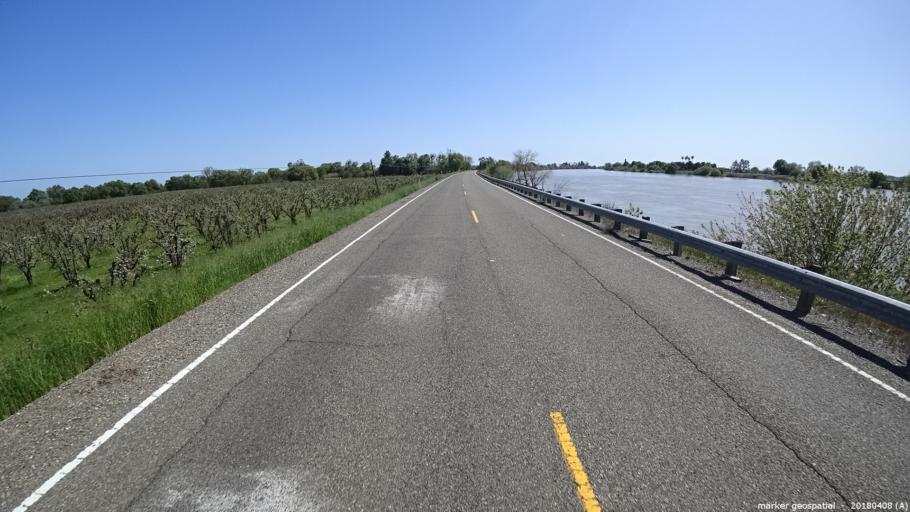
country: US
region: California
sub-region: Sacramento County
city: Laguna
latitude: 38.4025
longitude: -121.5129
